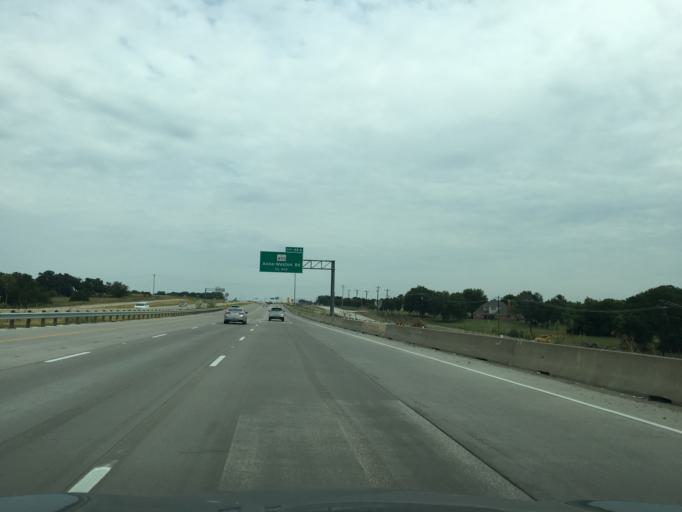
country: US
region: Texas
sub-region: Collin County
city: Anna
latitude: 33.3298
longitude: -96.5893
